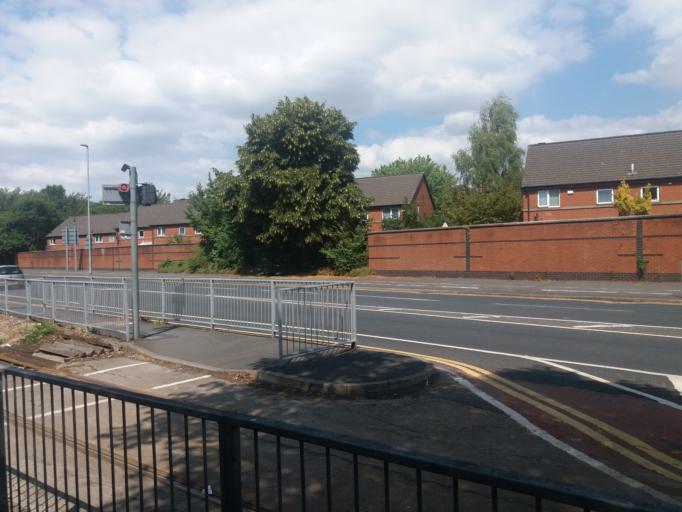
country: GB
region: England
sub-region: Lancashire
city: Preston
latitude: 53.7556
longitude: -2.7173
